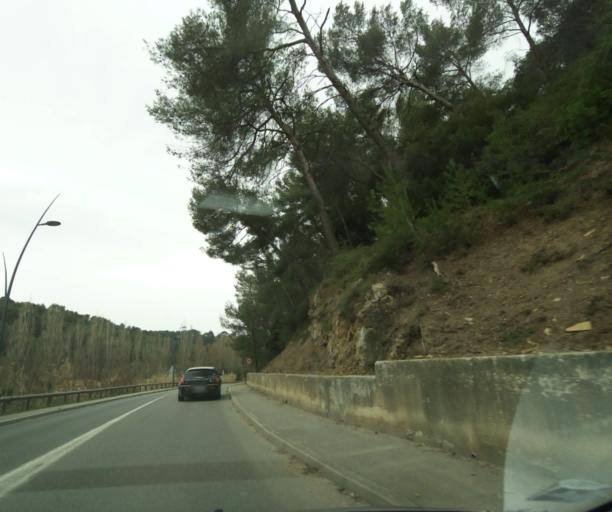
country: FR
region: Provence-Alpes-Cote d'Azur
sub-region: Departement des Bouches-du-Rhone
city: Saint-Marc-Jaumegarde
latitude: 43.5379
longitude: 5.4844
